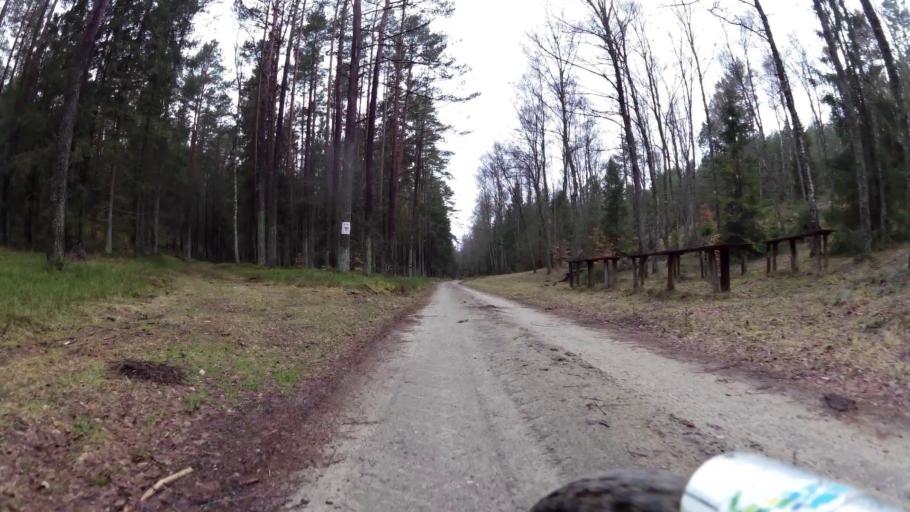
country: PL
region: Pomeranian Voivodeship
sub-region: Powiat bytowski
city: Borzytuchom
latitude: 54.2586
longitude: 17.3235
